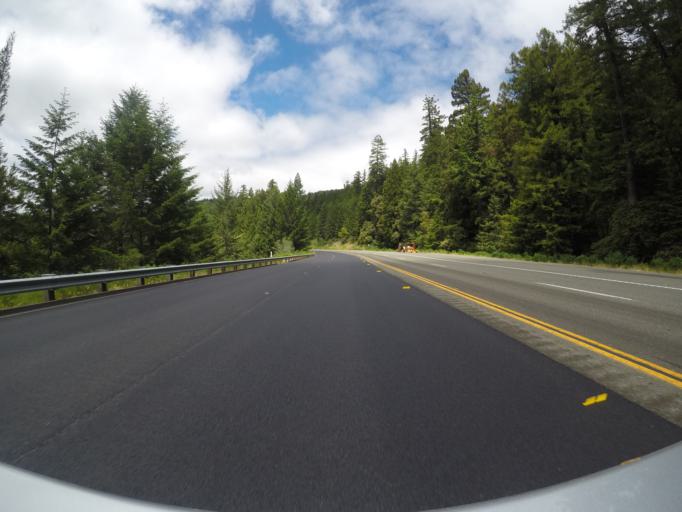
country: US
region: California
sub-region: Humboldt County
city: Redway
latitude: 40.2974
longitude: -123.8925
